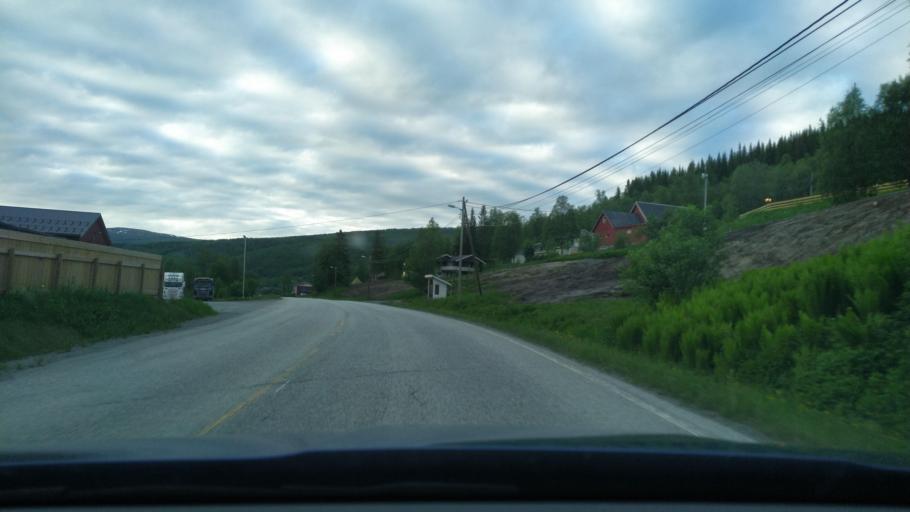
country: NO
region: Troms
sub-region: Sorreisa
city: Sorreisa
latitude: 69.1138
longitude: 18.2166
